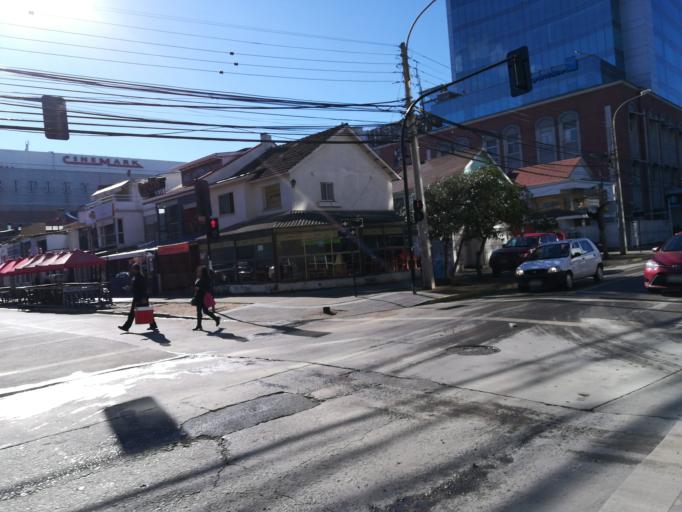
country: CL
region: Valparaiso
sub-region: Provincia de Valparaiso
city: Vina del Mar
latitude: -33.0104
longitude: -71.5477
